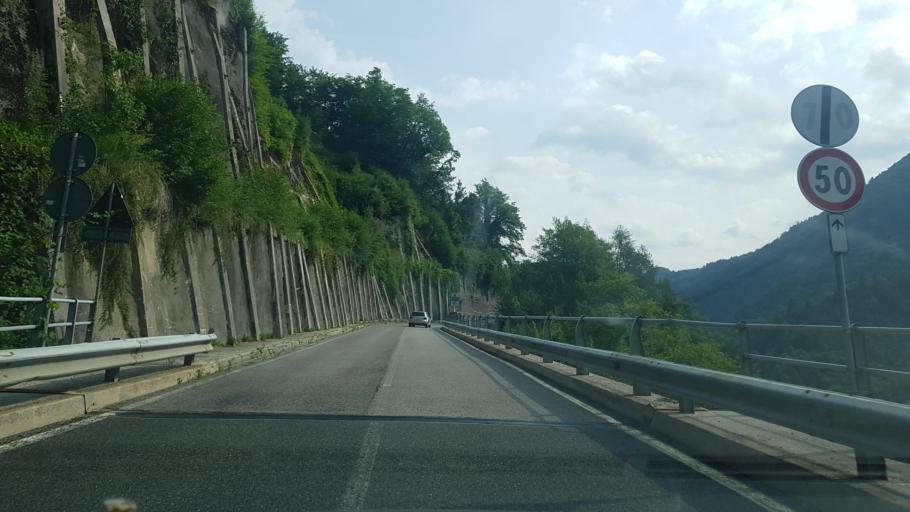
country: IT
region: Friuli Venezia Giulia
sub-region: Provincia di Udine
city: Paularo
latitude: 46.4853
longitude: 13.0933
